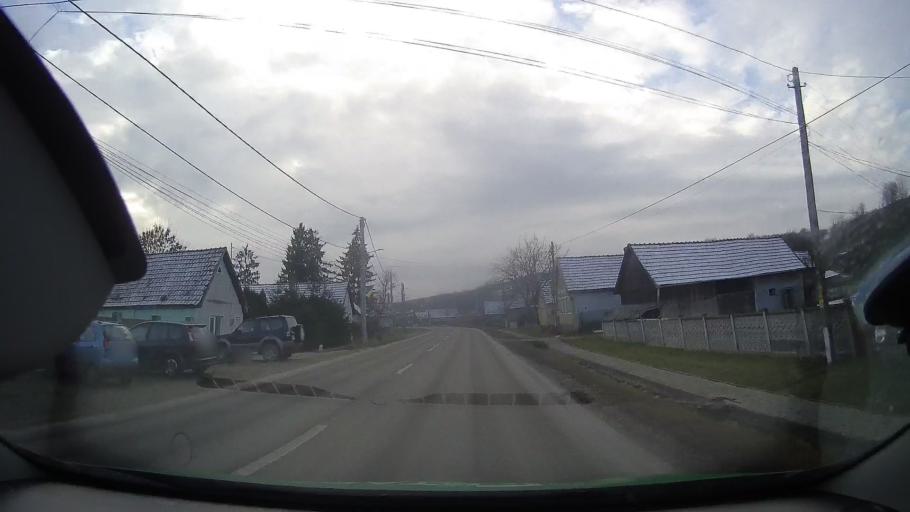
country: RO
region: Mures
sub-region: Comuna Cucerdea
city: Cucerdea
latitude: 46.4066
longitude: 24.2659
